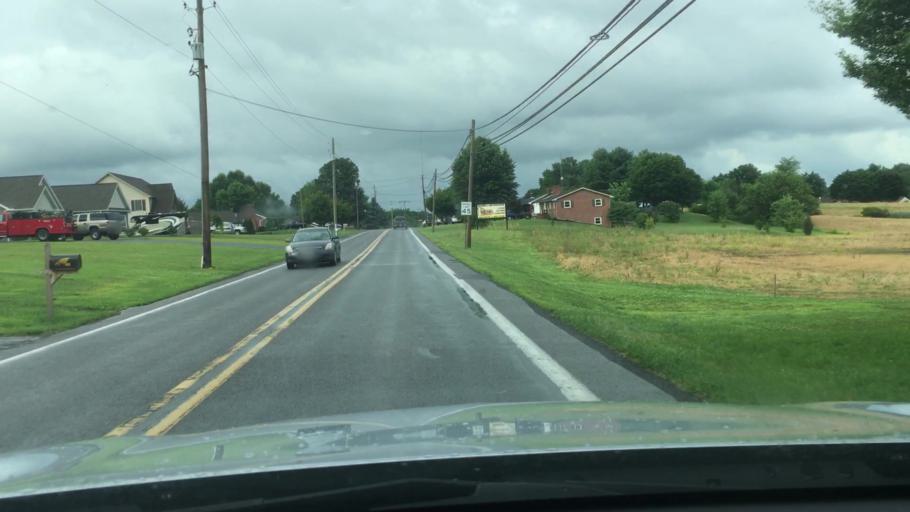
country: US
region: Pennsylvania
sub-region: Franklin County
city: Chambersburg
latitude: 39.9175
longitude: -77.7031
